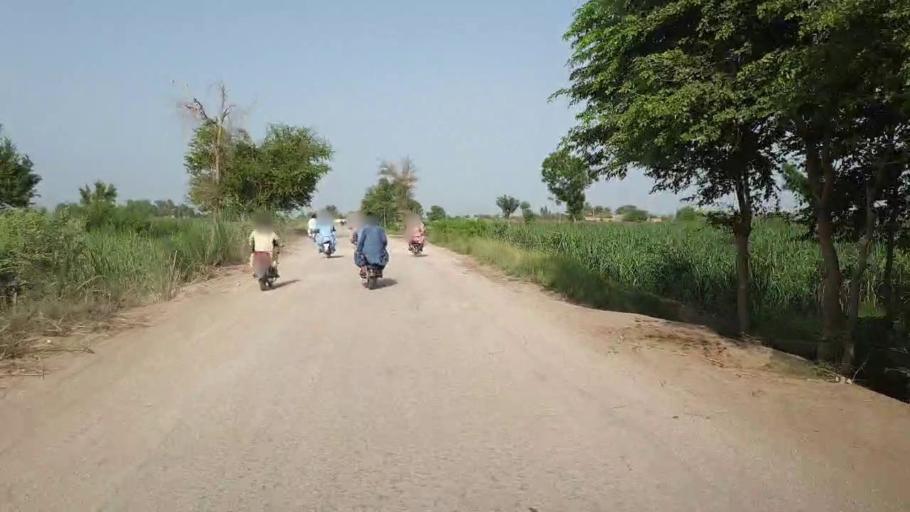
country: PK
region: Sindh
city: Daur
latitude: 26.3482
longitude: 68.1659
